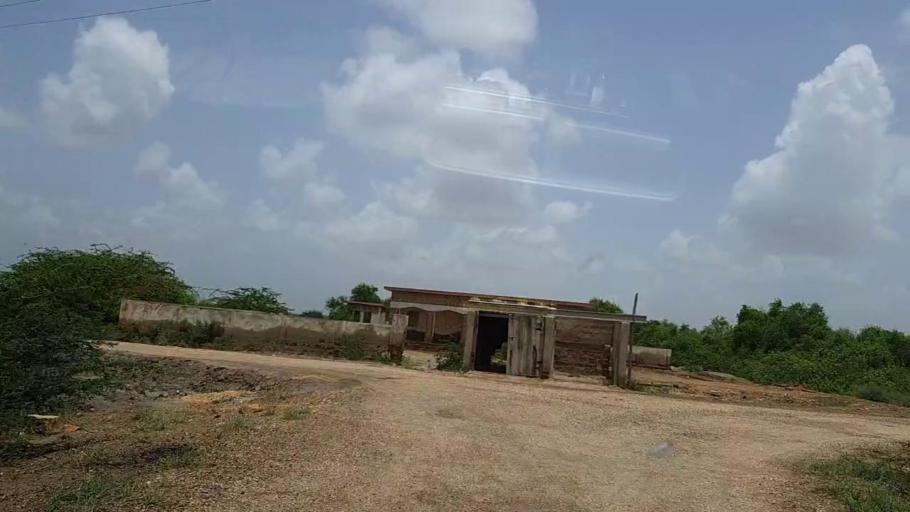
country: PK
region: Sindh
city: Keti Bandar
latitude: 24.1657
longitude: 67.5454
